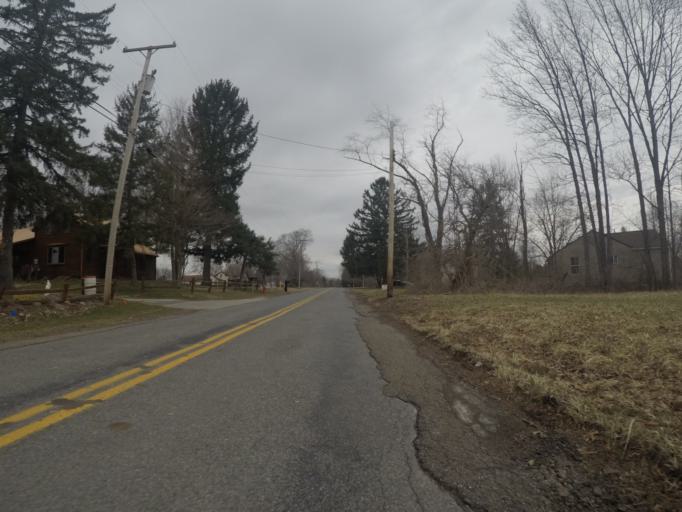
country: US
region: Ohio
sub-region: Portage County
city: Ravenna
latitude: 41.1760
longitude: -81.2928
